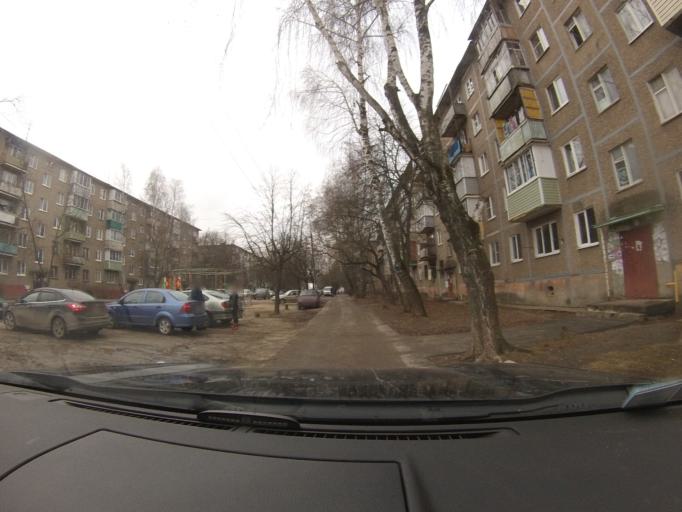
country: RU
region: Moskovskaya
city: Lopatinskiy
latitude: 55.3450
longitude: 38.7227
